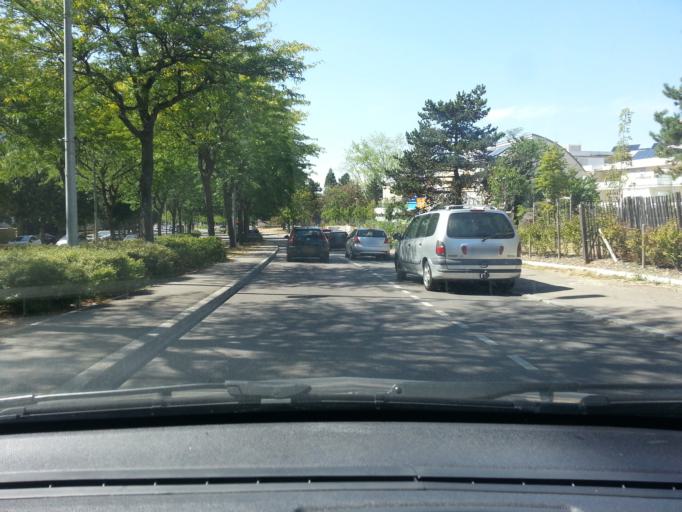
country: FR
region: Bourgogne
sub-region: Departement de la Cote-d'Or
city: Saint-Apollinaire
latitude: 47.3348
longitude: 5.0662
